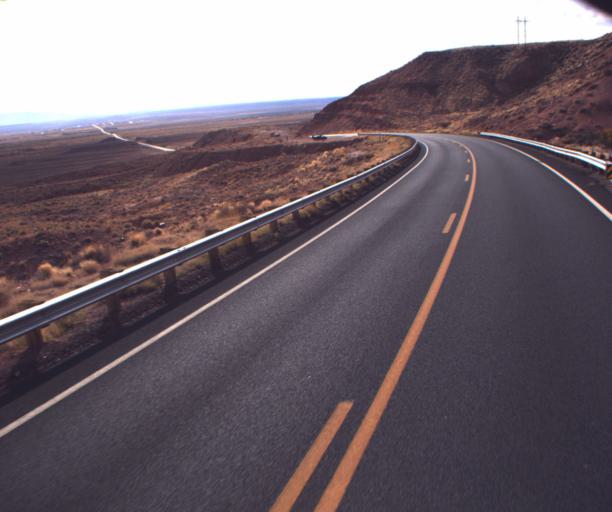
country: US
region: Arizona
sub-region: Apache County
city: Many Farms
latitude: 36.5466
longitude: -109.5306
